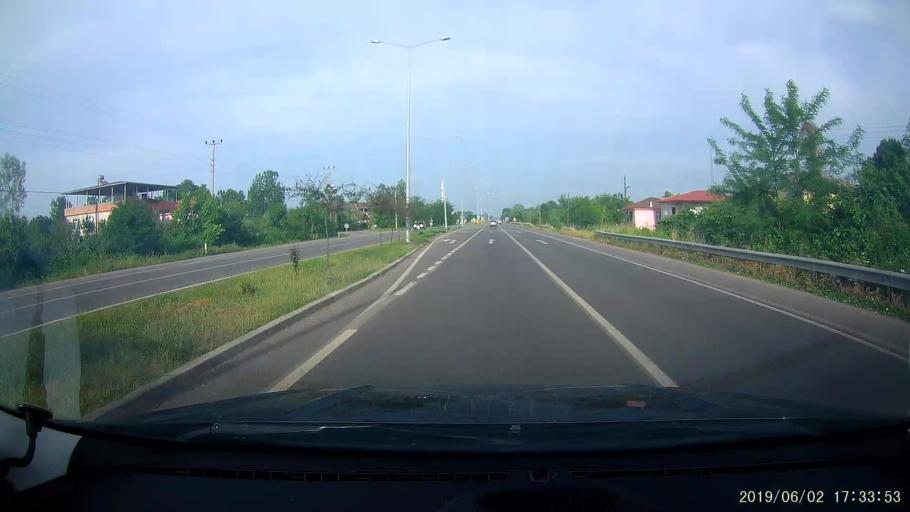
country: TR
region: Samsun
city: Terme
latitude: 41.2206
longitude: 36.8580
